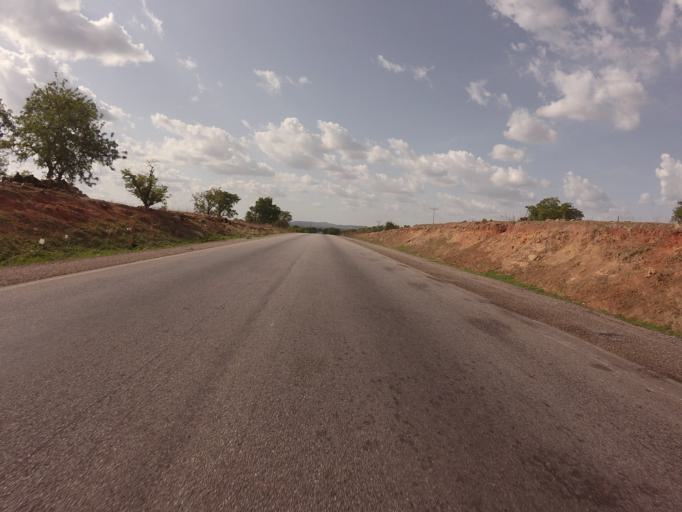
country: GH
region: Upper East
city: Bolgatanga
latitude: 10.5718
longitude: -0.8330
